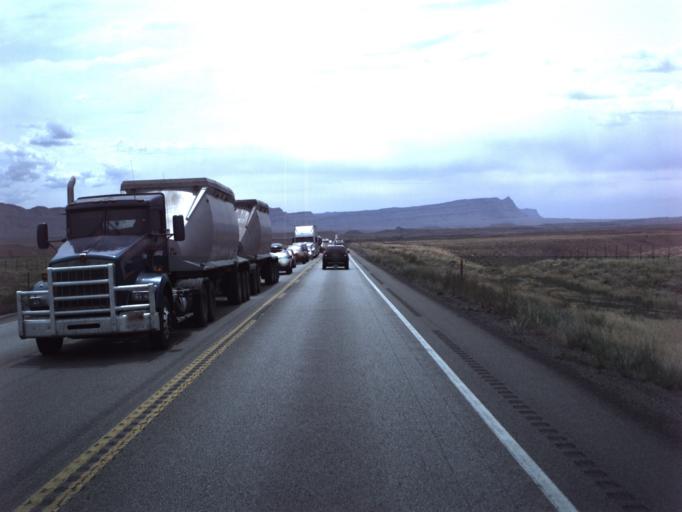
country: US
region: Utah
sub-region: Carbon County
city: East Carbon City
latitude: 39.3900
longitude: -110.4142
